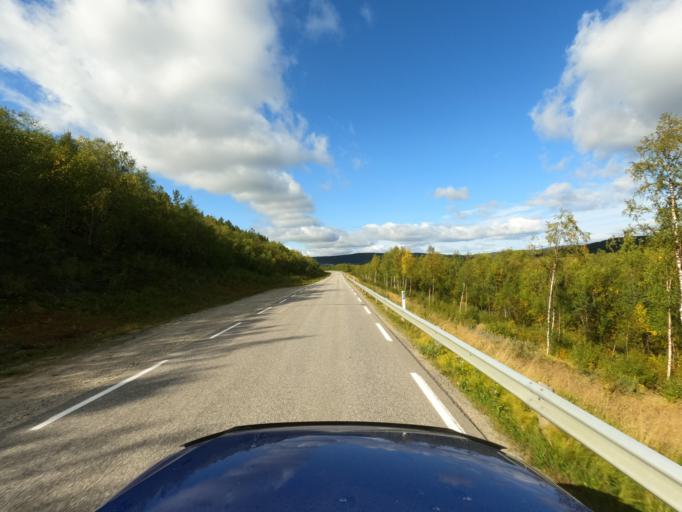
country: NO
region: Finnmark Fylke
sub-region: Karasjok
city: Karasjohka
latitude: 69.4558
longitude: 25.5660
